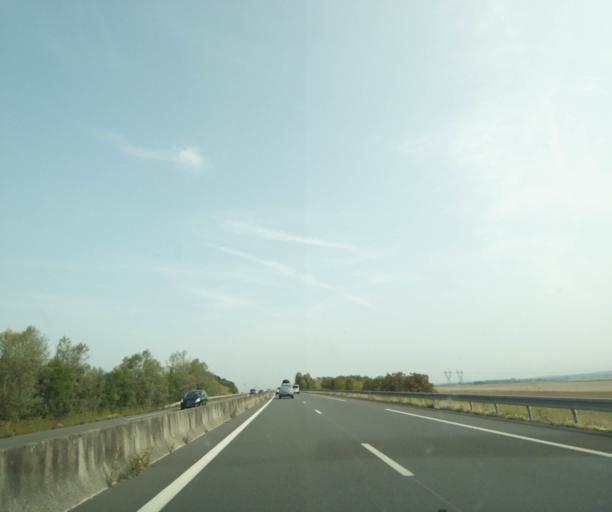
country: FR
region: Pays de la Loire
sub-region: Departement de la Sarthe
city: Arconnay
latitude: 48.3690
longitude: 0.1019
